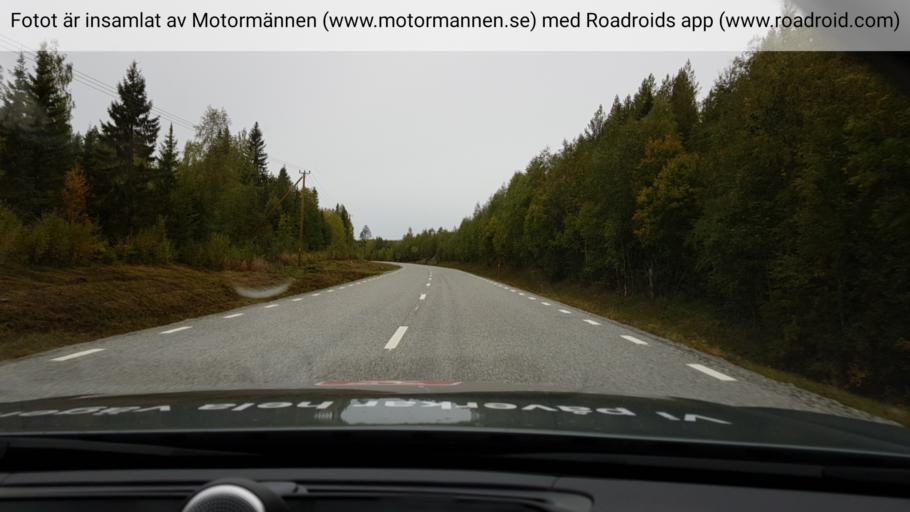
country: SE
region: Jaemtland
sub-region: Stroemsunds Kommun
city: Stroemsund
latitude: 64.1935
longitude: 15.6314
